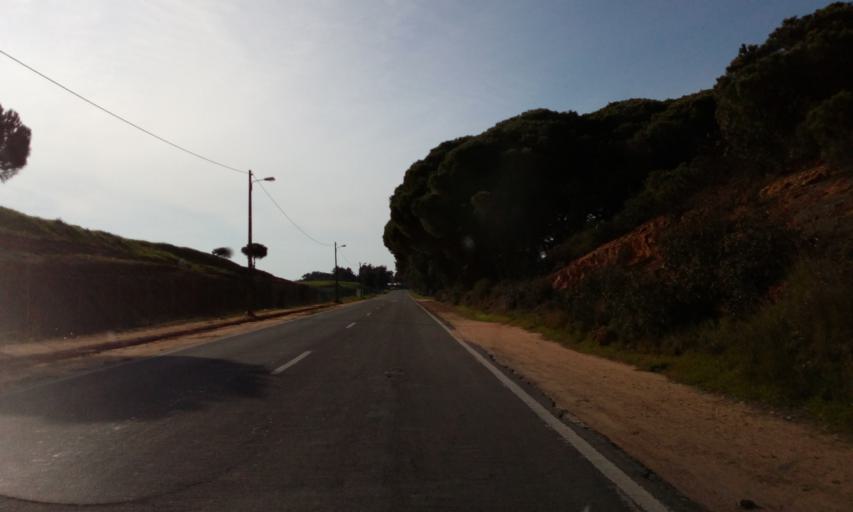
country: PT
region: Faro
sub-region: Faro
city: Faro
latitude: 37.0209
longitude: -7.9816
